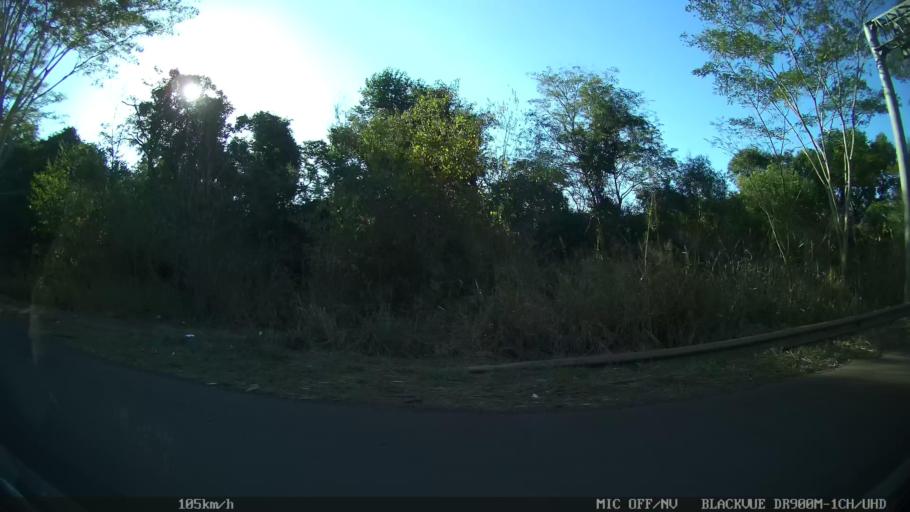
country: BR
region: Sao Paulo
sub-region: Guapiacu
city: Guapiacu
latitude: -20.7430
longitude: -49.1051
